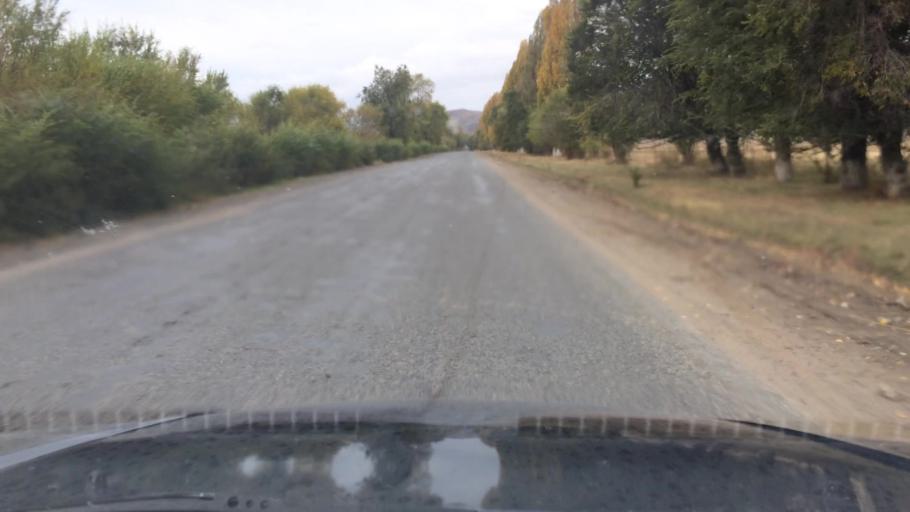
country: KG
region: Ysyk-Koel
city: Pokrovka
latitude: 42.7374
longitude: 77.9283
